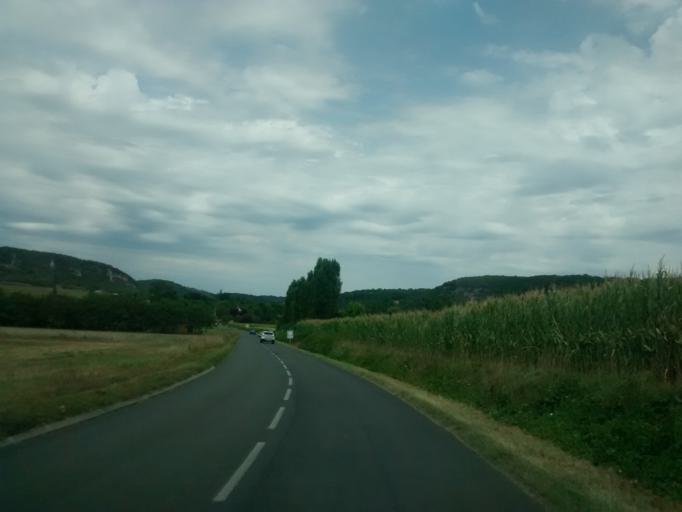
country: FR
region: Aquitaine
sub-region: Departement de la Dordogne
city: Cenac-et-Saint-Julien
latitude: 44.8270
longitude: 1.1601
